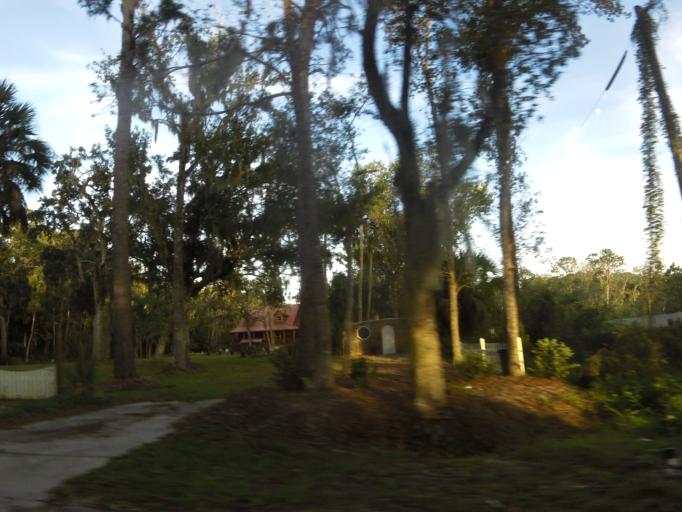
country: US
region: Florida
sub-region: Saint Johns County
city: Palm Valley
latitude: 30.1733
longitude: -81.3945
